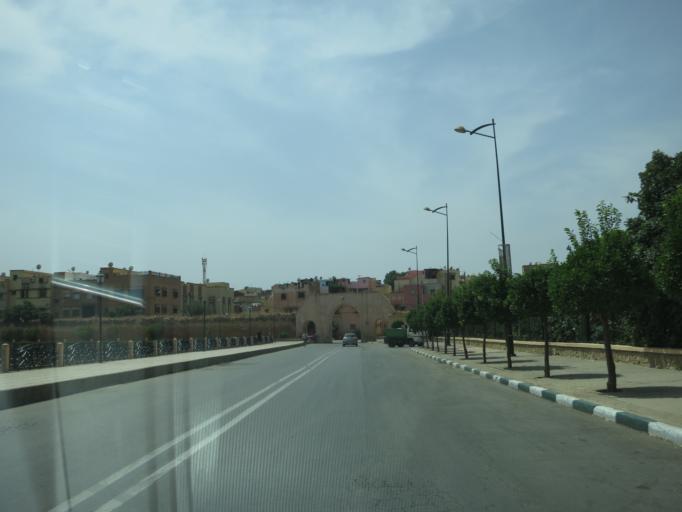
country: MA
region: Meknes-Tafilalet
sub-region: Meknes
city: Meknes
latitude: 33.8829
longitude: -5.5611
